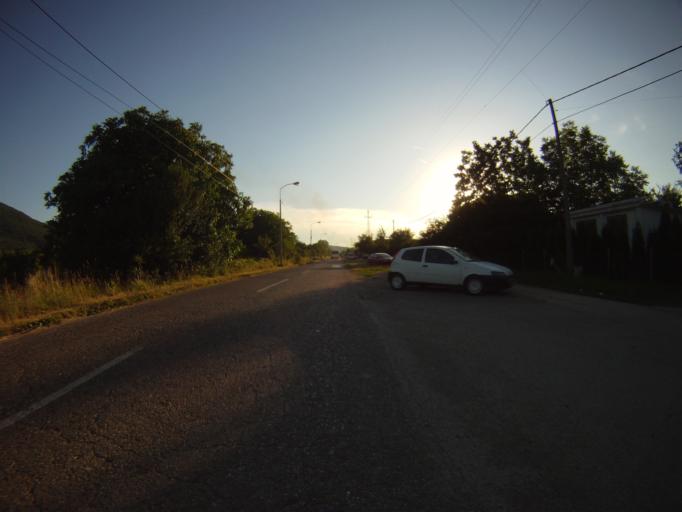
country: RS
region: Central Serbia
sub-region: Nisavski Okrug
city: Niska Banja
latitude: 43.3004
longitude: 22.0153
